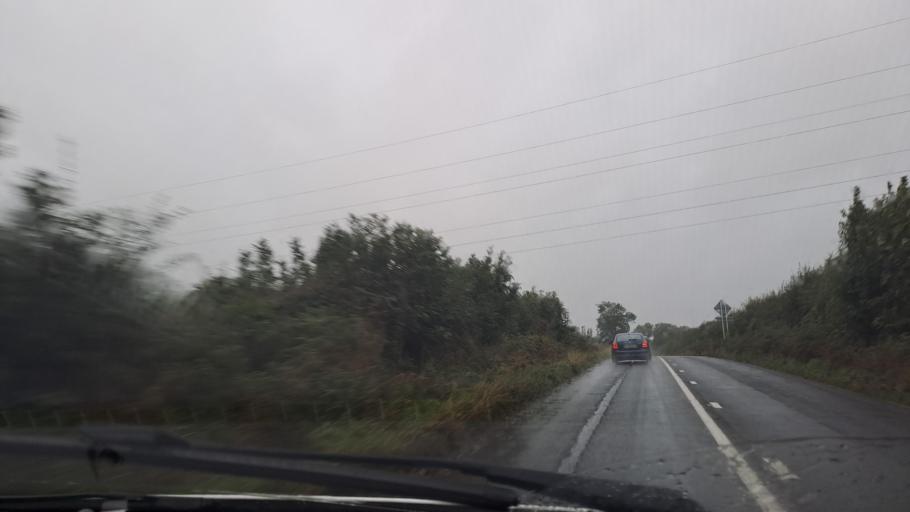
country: IE
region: Leinster
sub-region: Lu
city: Dundalk
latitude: 53.9935
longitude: -6.4530
